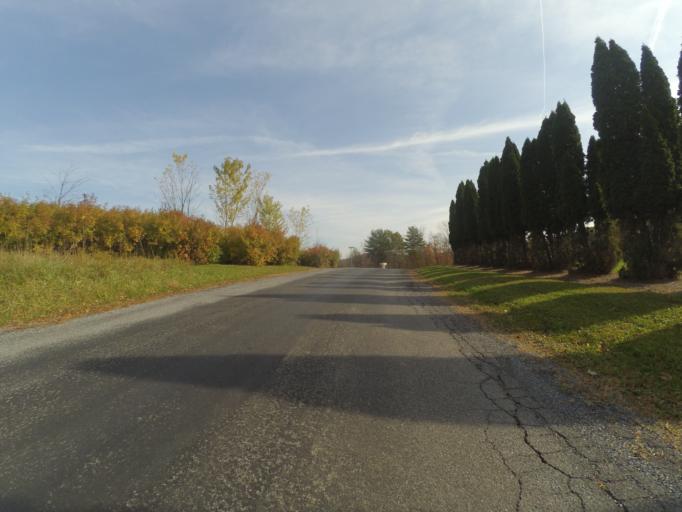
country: US
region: Pennsylvania
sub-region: Centre County
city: Park Forest Village
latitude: 40.9191
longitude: -77.9101
